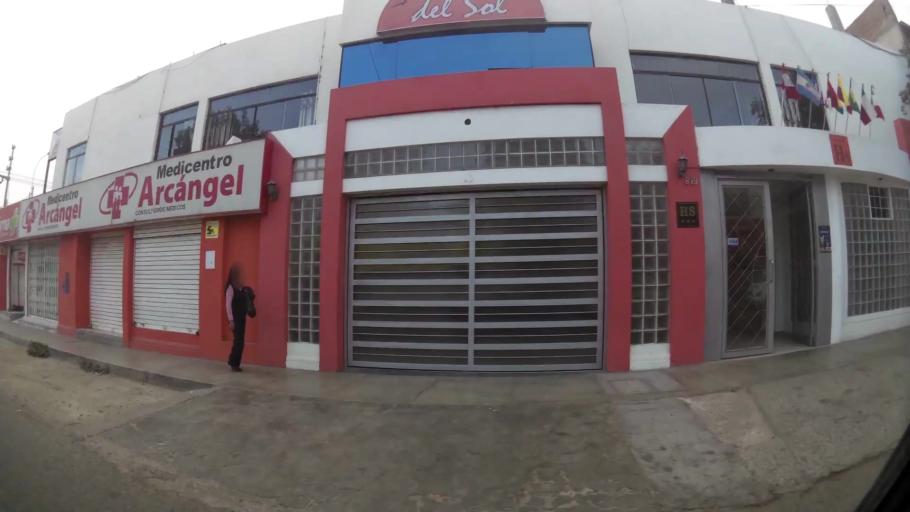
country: PE
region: La Libertad
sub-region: Provincia de Trujillo
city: Trujillo
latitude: -8.0989
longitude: -79.0279
